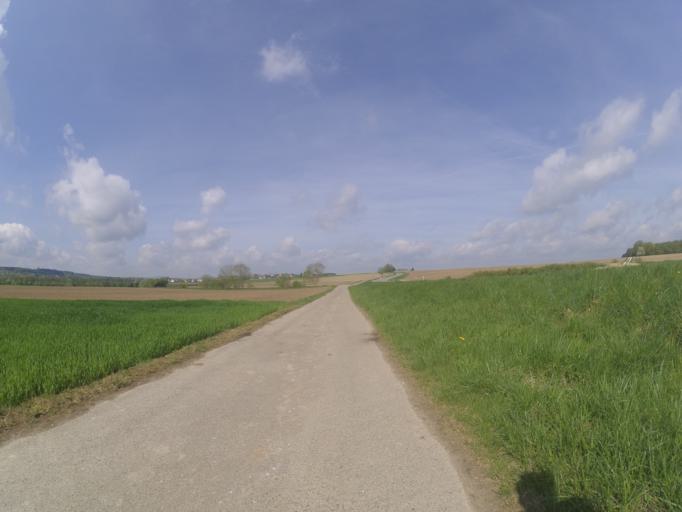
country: DE
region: Baden-Wuerttemberg
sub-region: Tuebingen Region
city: Griesingen
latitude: 48.2437
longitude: 9.7822
